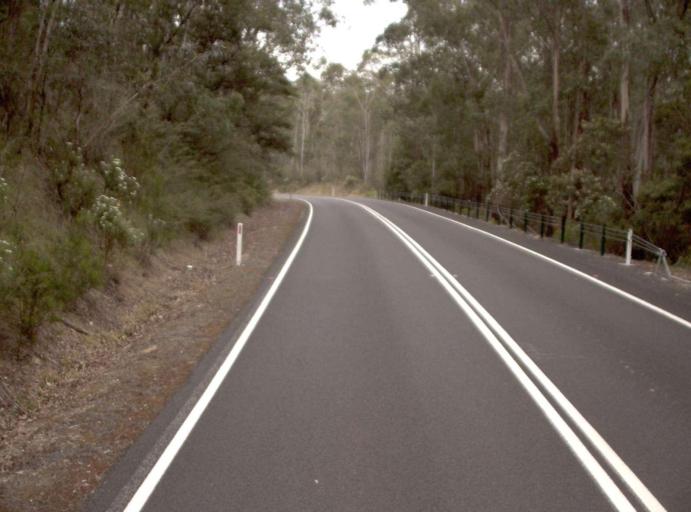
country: AU
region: New South Wales
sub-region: Bombala
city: Bombala
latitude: -37.3626
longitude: 149.2027
